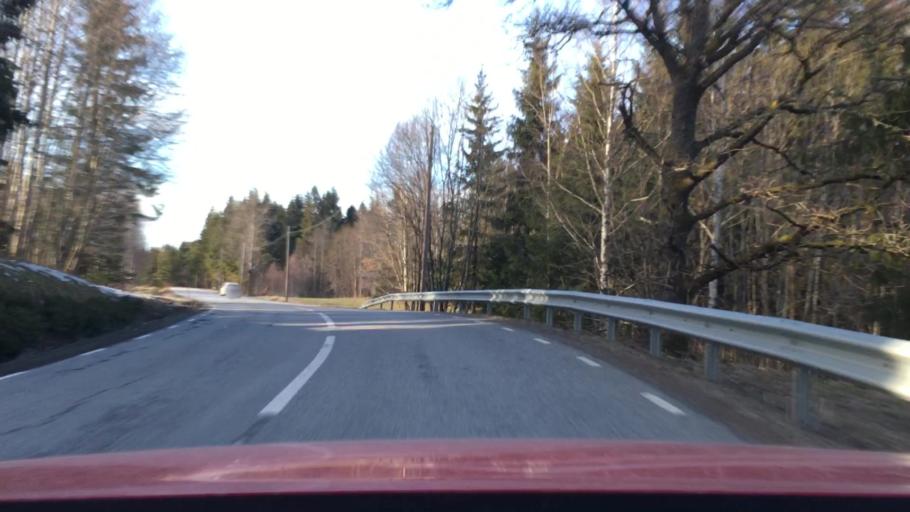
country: SE
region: Vaestra Goetaland
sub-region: Tanums Kommun
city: Tanumshede
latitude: 58.8092
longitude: 11.5516
